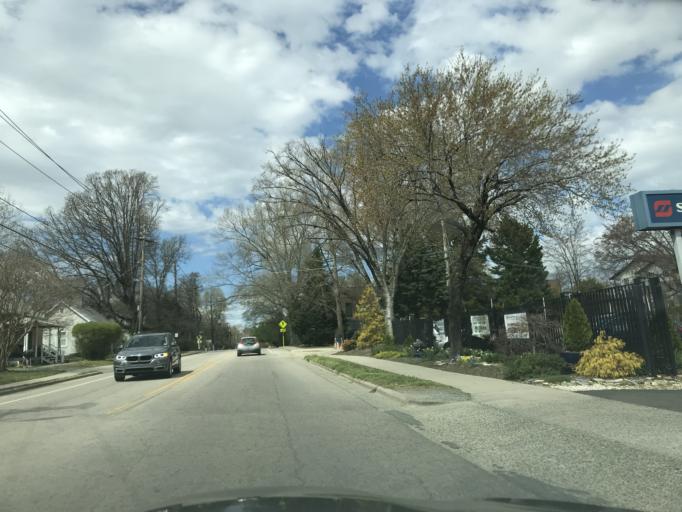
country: US
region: North Carolina
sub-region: Orange County
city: Carrboro
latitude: 35.9130
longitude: -79.0722
